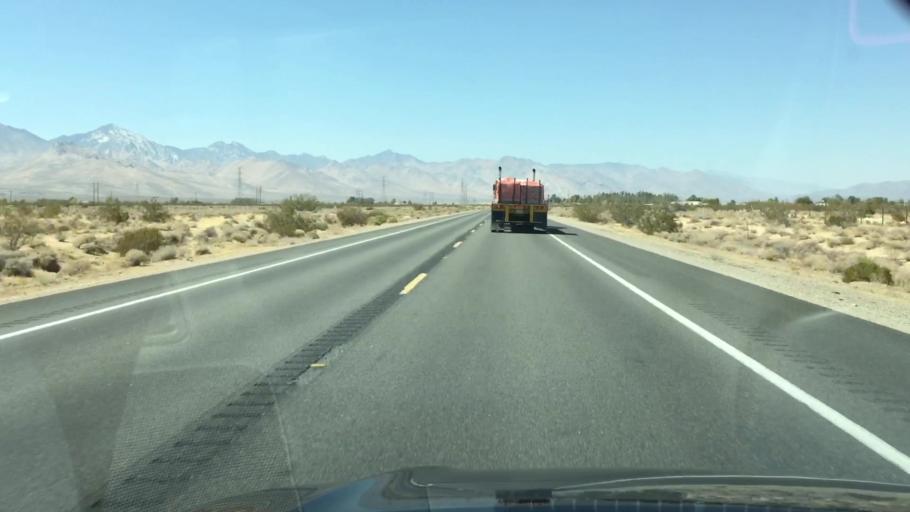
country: US
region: California
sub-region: Kern County
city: China Lake Acres
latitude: 35.6297
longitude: -117.7818
